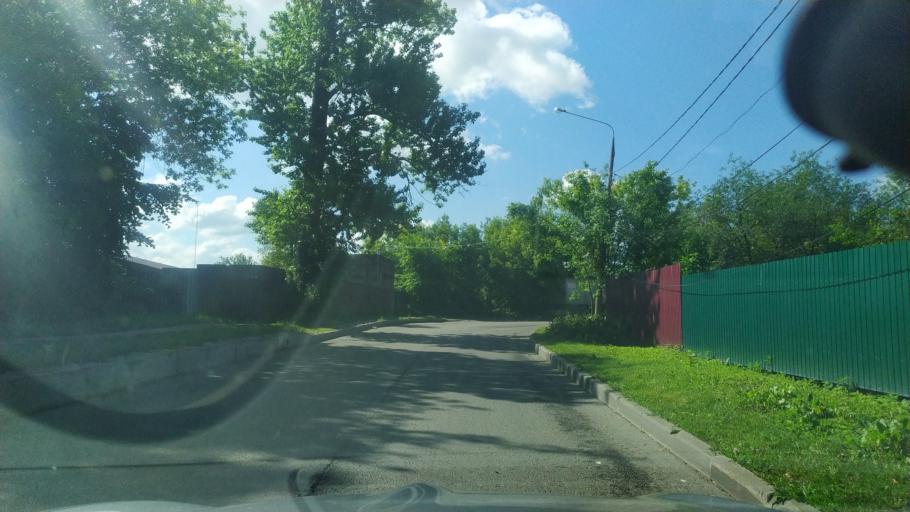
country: RU
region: Moscow
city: Vostochnyy
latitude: 55.8147
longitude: 37.8658
